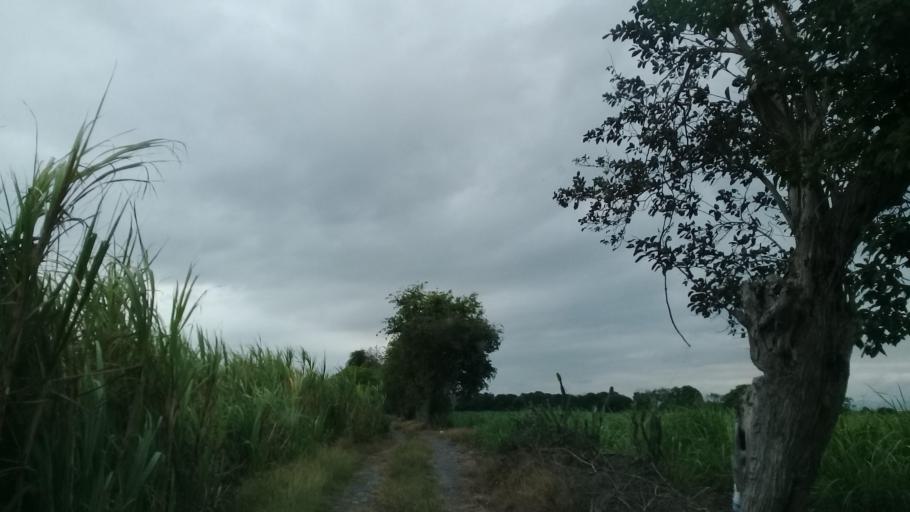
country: MX
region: Veracruz
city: Ursulo Galvan
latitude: 19.3830
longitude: -96.3588
